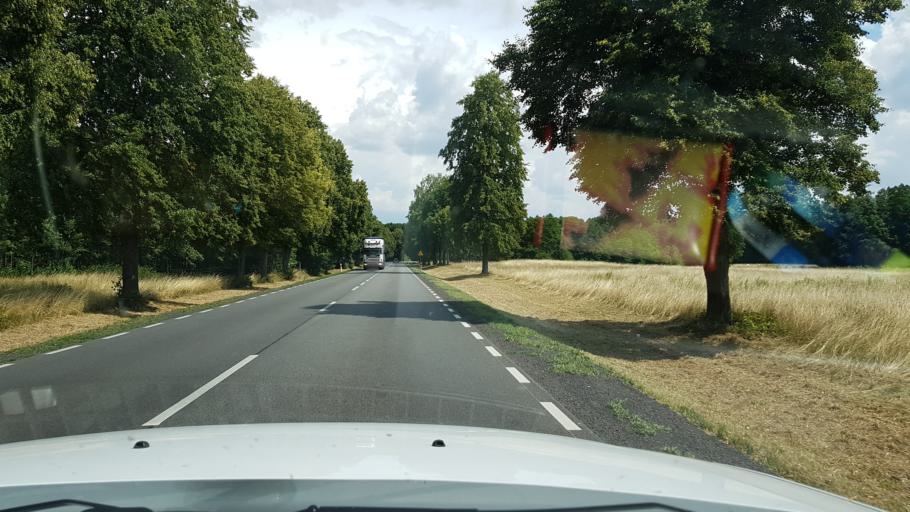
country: PL
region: West Pomeranian Voivodeship
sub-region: Powiat walecki
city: Walcz
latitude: 53.3059
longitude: 16.3998
